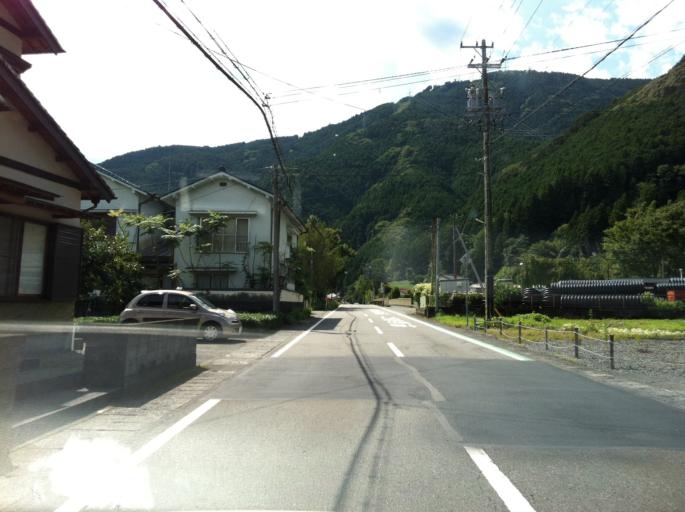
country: JP
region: Shizuoka
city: Kanaya
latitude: 35.0619
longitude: 138.0950
